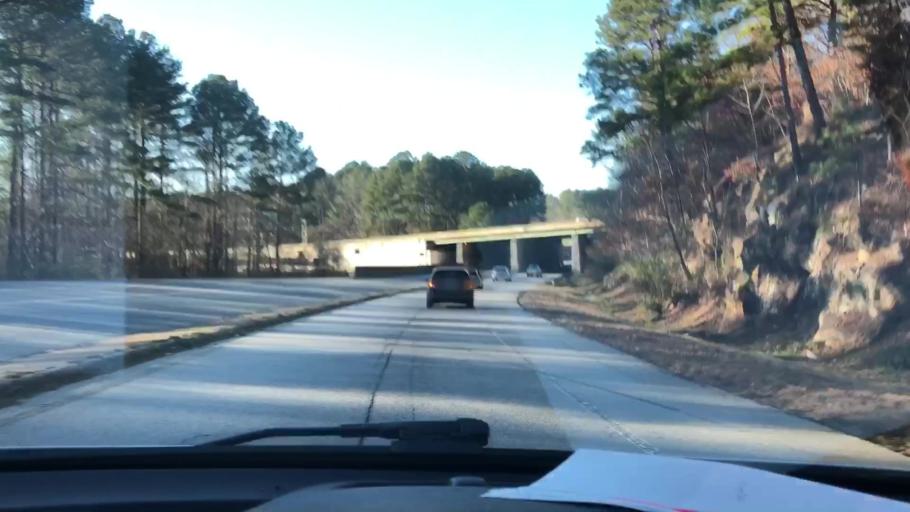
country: US
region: Georgia
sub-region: DeKalb County
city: Stone Mountain
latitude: 33.8231
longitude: -84.1510
